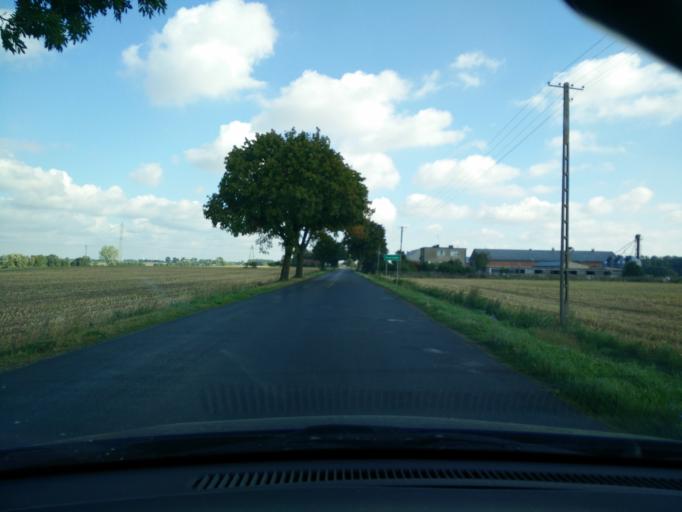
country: PL
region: Greater Poland Voivodeship
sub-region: Powiat sredzki
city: Dominowo
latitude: 52.2910
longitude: 17.3319
